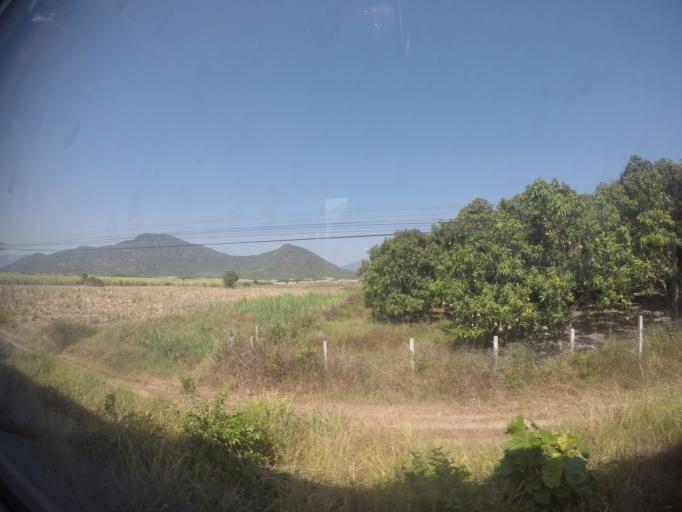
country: VN
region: Khanh Hoa
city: Cam Lam
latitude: 12.0084
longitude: 109.1209
